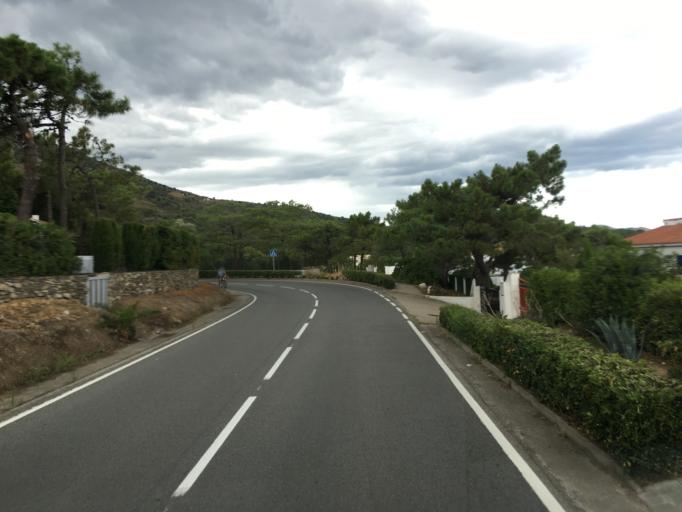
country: ES
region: Catalonia
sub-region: Provincia de Girona
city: Llanca
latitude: 42.3413
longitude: 3.1880
